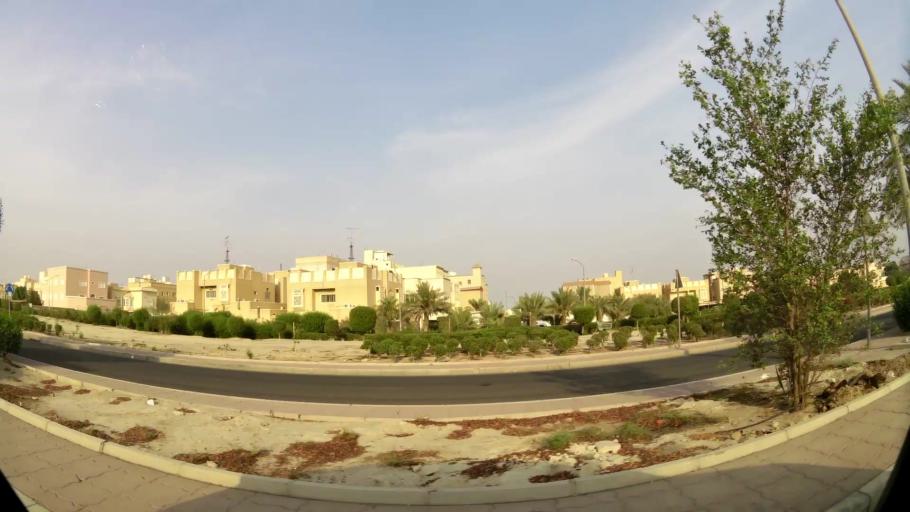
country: KW
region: Mubarak al Kabir
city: Mubarak al Kabir
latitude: 29.1842
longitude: 48.0727
